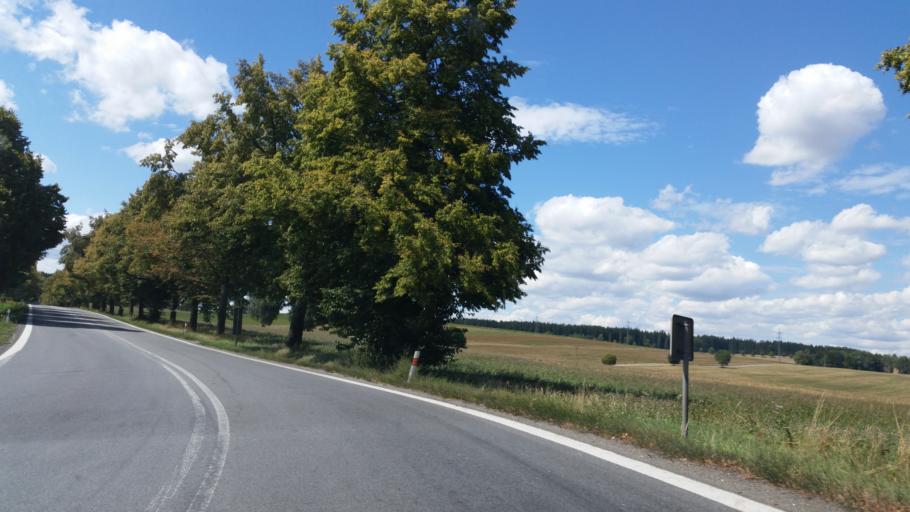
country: CZ
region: Vysocina
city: Cernovice
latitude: 49.4271
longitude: 14.9300
